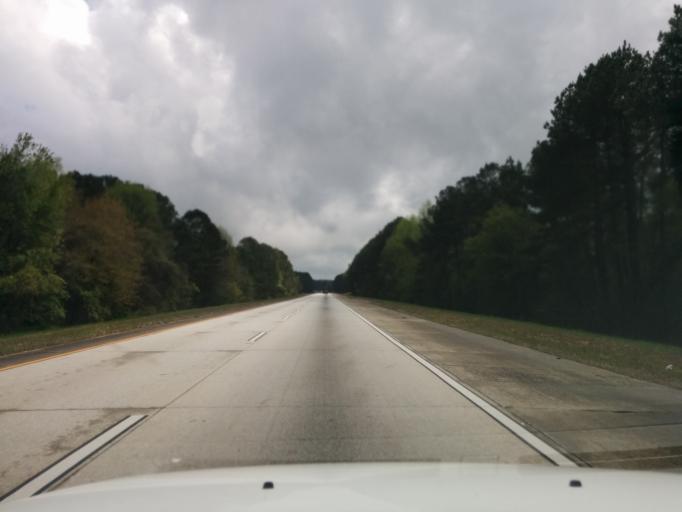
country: US
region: Georgia
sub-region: Candler County
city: Metter
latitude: 32.3302
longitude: -81.9375
